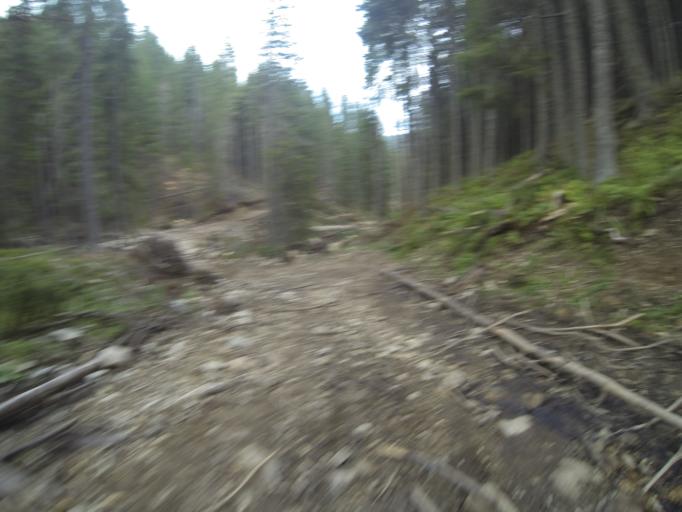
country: RO
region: Gorj
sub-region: Comuna Polovragi
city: Polovragi
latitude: 45.2979
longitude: 23.8405
